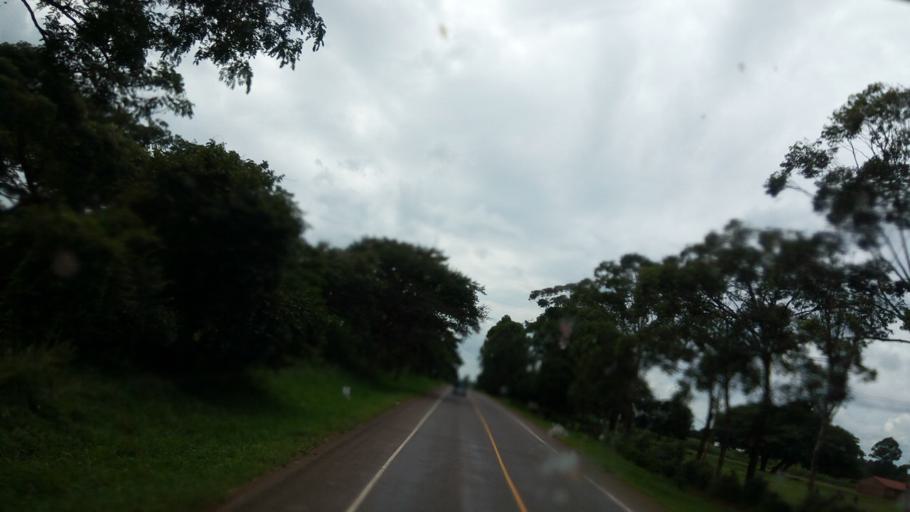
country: UG
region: Western Region
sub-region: Kiryandongo District
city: Kiryandongo
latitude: 2.0809
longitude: 32.1937
